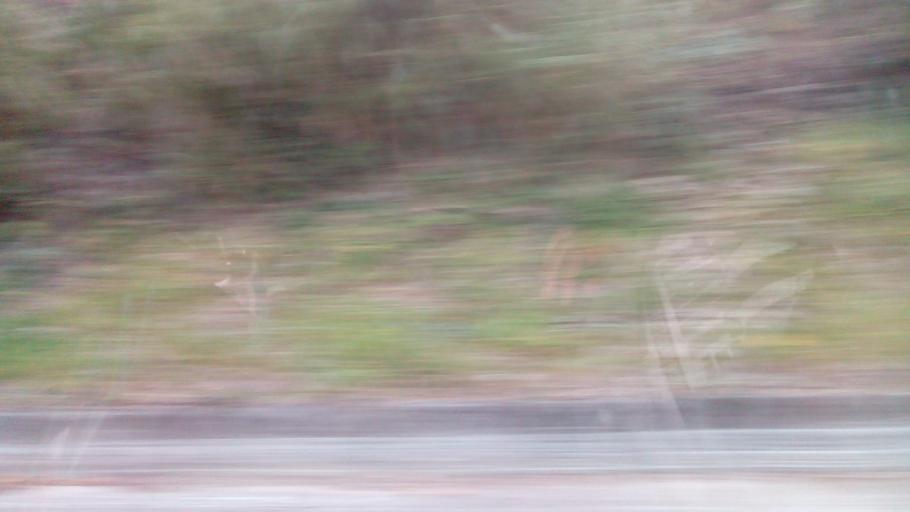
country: TW
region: Taiwan
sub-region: Hualien
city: Hualian
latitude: 24.3538
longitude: 121.3250
